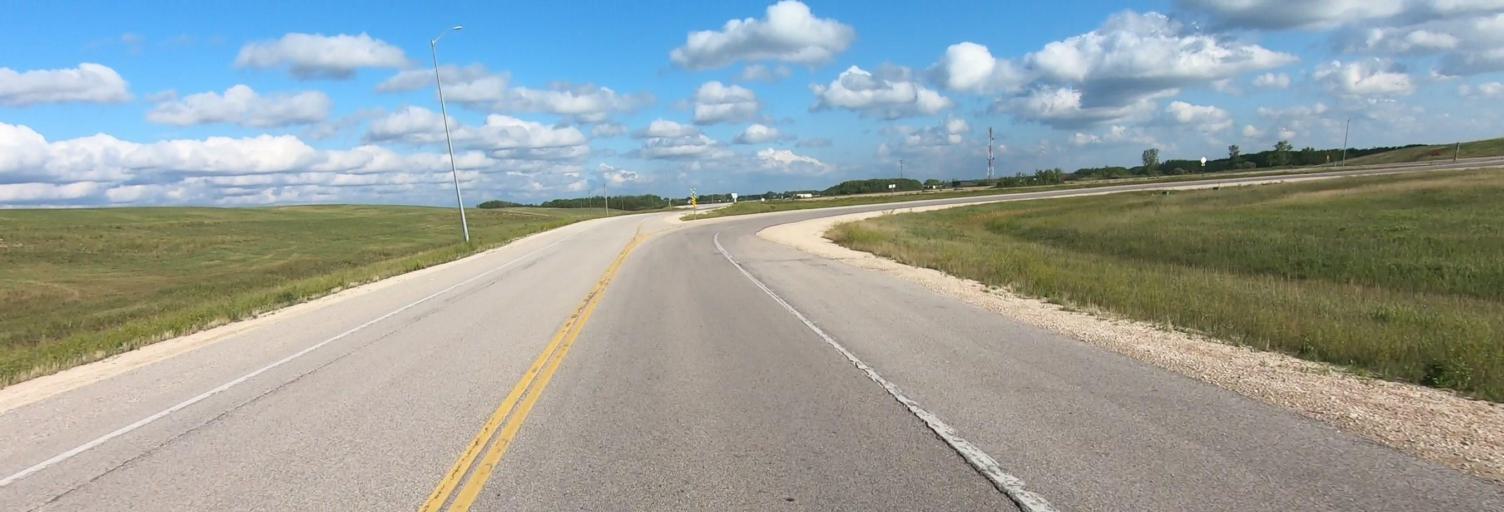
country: CA
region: Manitoba
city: Selkirk
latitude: 50.0873
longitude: -96.9230
